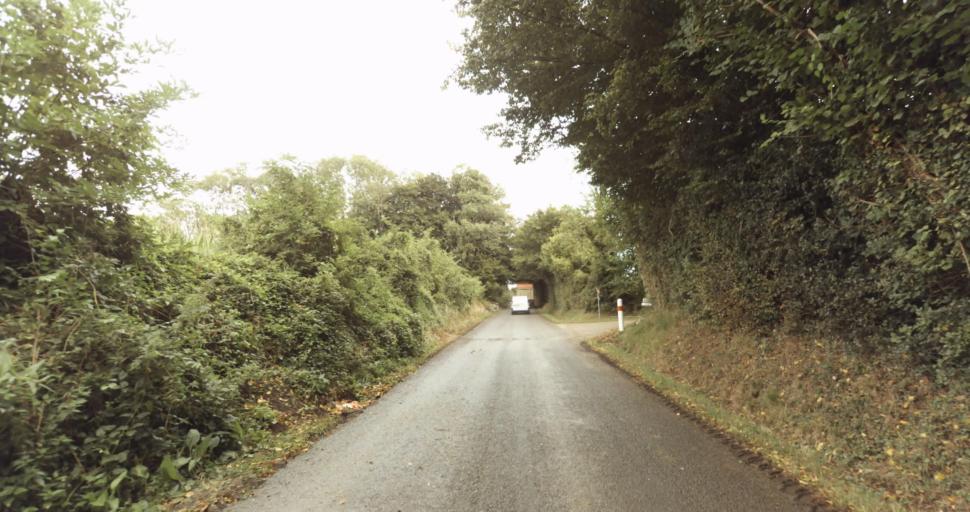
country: FR
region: Lower Normandy
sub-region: Departement de l'Orne
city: Vimoutiers
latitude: 48.8556
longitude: 0.2254
